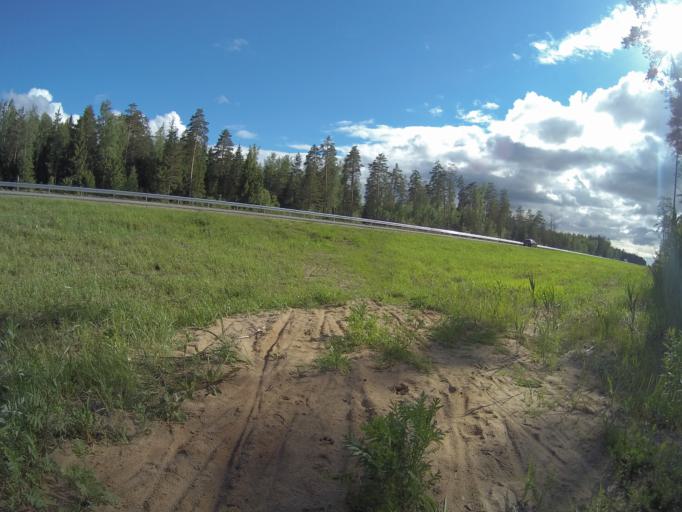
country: RU
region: Vladimir
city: Bogolyubovo
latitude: 56.0946
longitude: 40.5452
